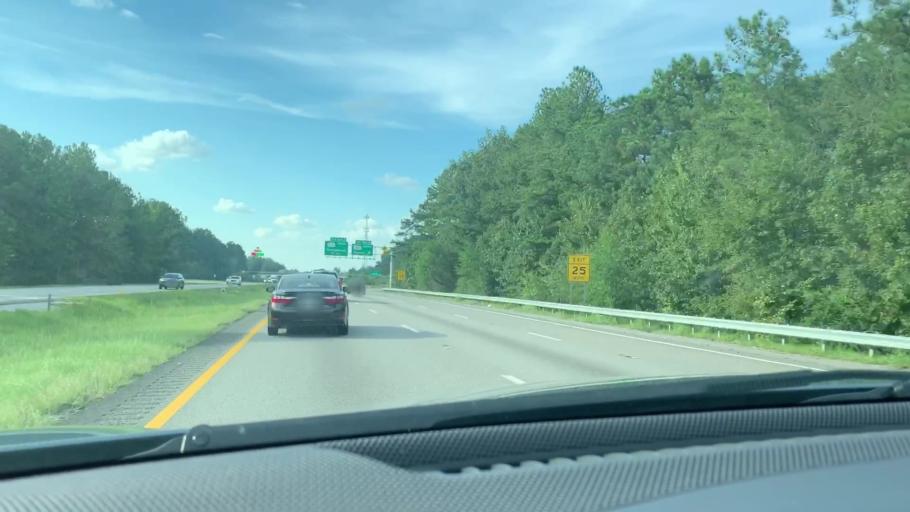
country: US
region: South Carolina
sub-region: Orangeburg County
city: Brookdale
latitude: 33.4549
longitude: -80.7262
